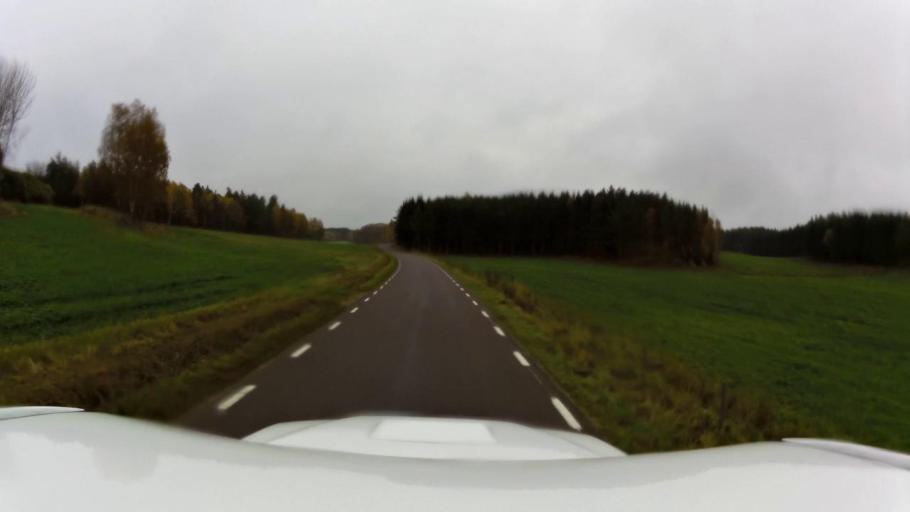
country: SE
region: OEstergoetland
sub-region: Linkopings Kommun
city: Linghem
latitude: 58.3587
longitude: 15.8425
